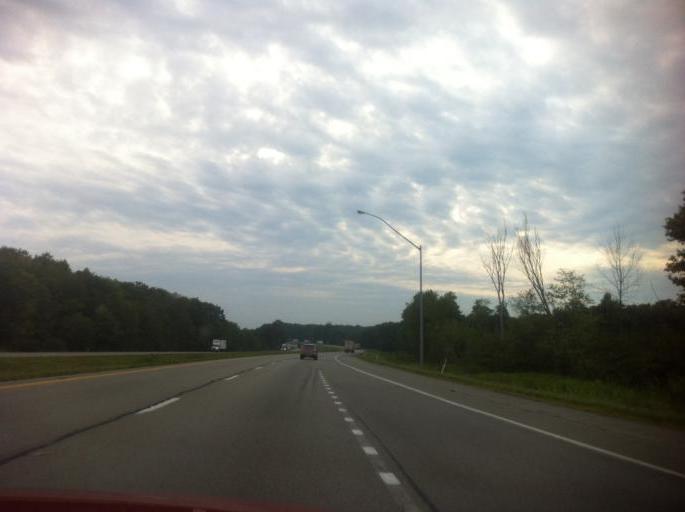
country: US
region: Pennsylvania
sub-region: Mercer County
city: Grove City
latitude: 41.2017
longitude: -79.9781
